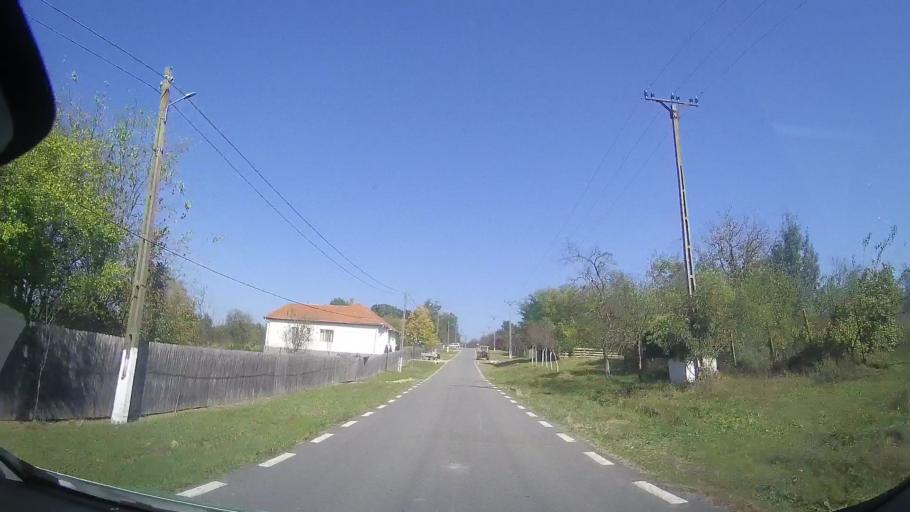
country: RO
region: Timis
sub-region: Comuna Ohaba Lunga
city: Ohaba Lunga
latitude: 45.9047
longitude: 21.9364
